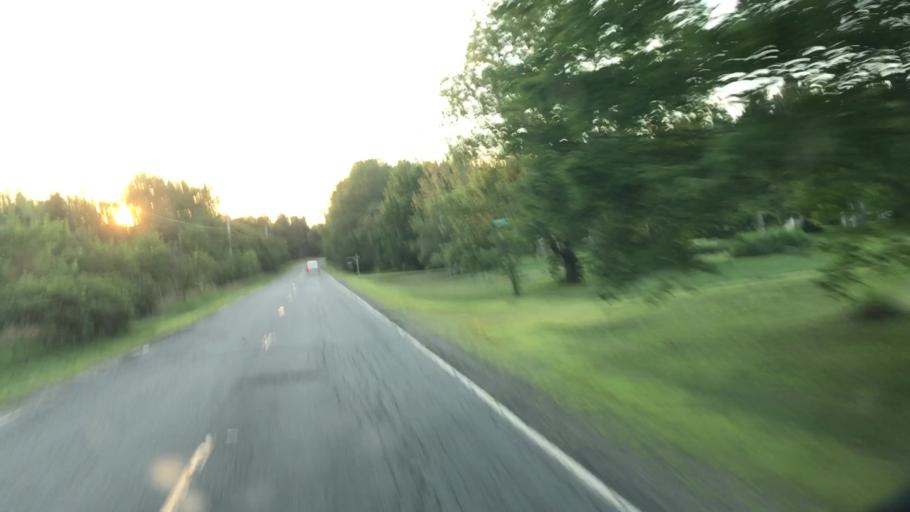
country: US
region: Maine
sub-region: Penobscot County
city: Medway
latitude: 45.5961
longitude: -68.2426
